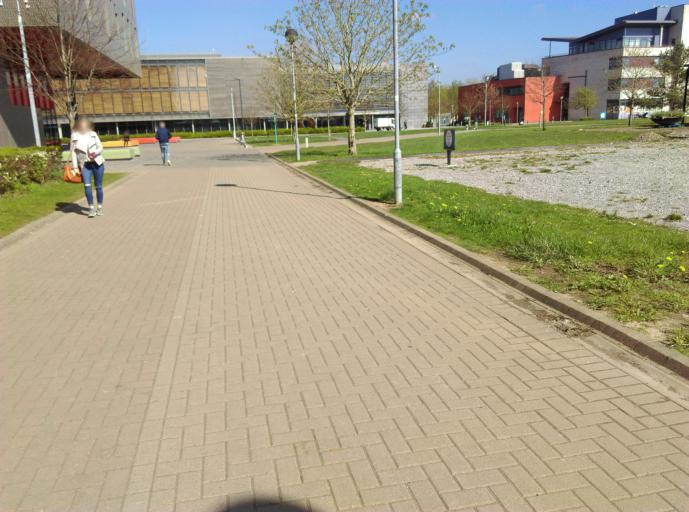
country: IE
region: Leinster
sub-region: Kildare
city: Maynooth
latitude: 53.3844
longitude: -6.6021
